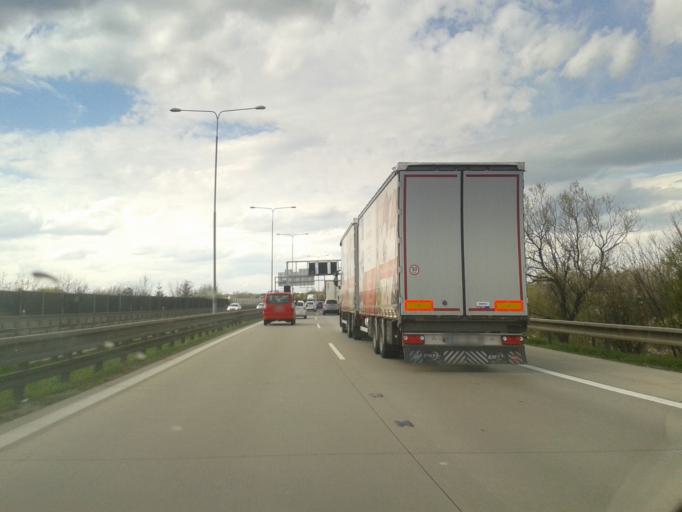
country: CZ
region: Central Bohemia
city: Trebotov
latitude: 50.0264
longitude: 14.2915
